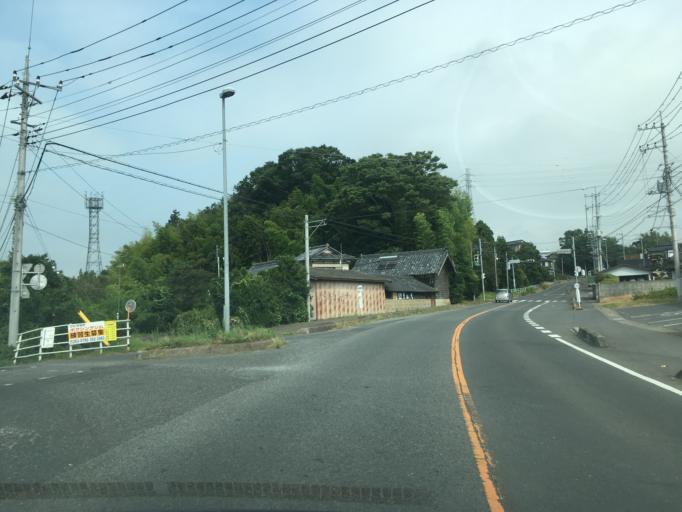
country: JP
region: Ibaraki
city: Oarai
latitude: 36.3515
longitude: 140.5721
